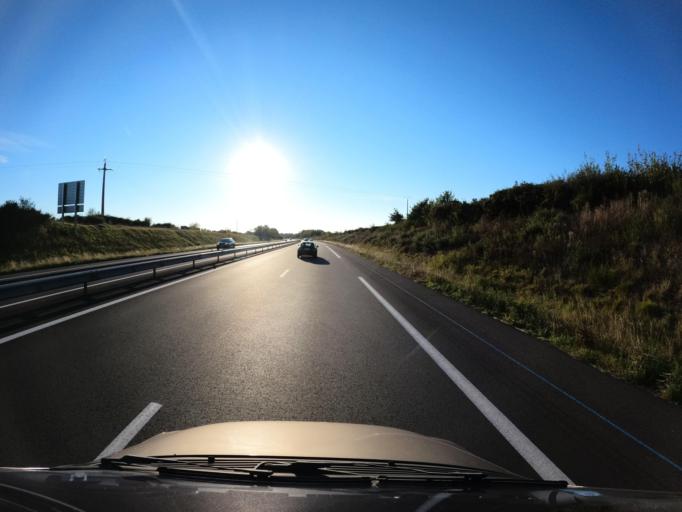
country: FR
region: Pays de la Loire
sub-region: Departement de la Vendee
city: Beaurepaire
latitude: 46.8961
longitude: -1.0811
